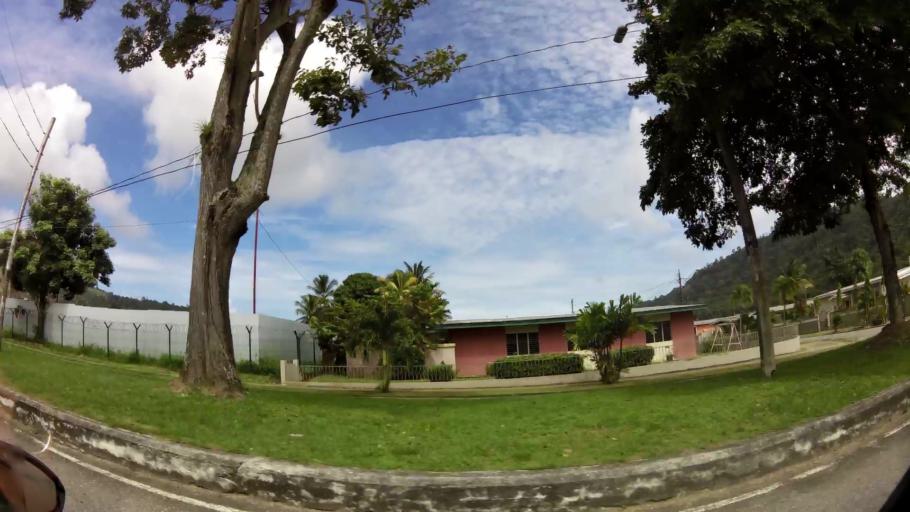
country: TT
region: Diego Martin
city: Petit Valley
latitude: 10.7179
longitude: -61.5584
